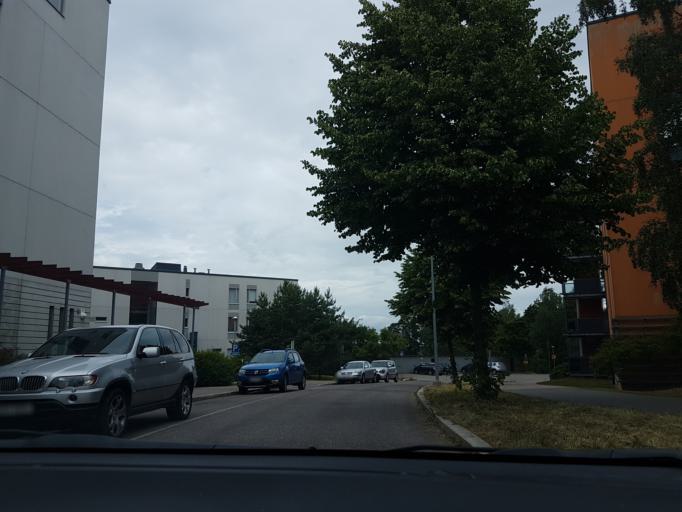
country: FI
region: Uusimaa
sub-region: Helsinki
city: Vantaa
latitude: 60.2329
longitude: 25.0573
